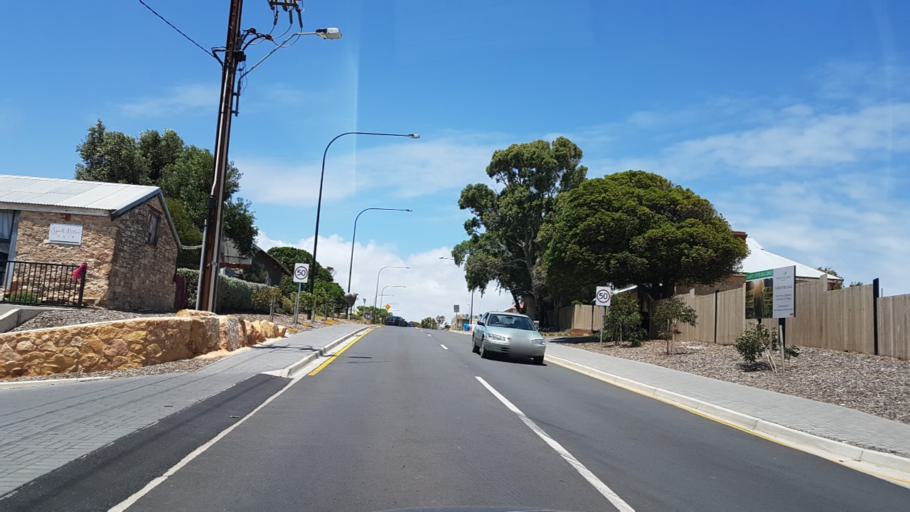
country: AU
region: South Australia
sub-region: Onkaparinga
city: Aldinga
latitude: -35.2655
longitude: 138.4830
